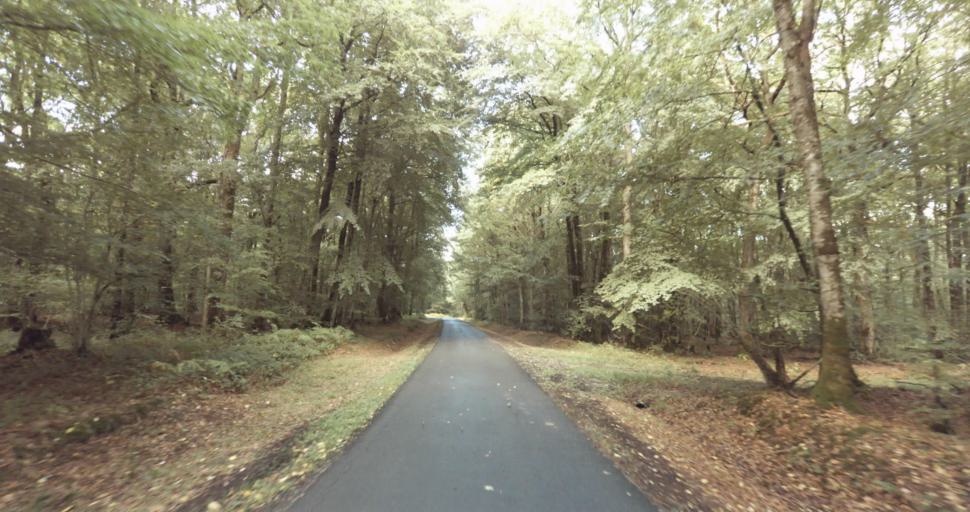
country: FR
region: Lower Normandy
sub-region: Departement de l'Orne
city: Sainte-Gauburge-Sainte-Colombe
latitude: 48.7571
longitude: 0.4151
